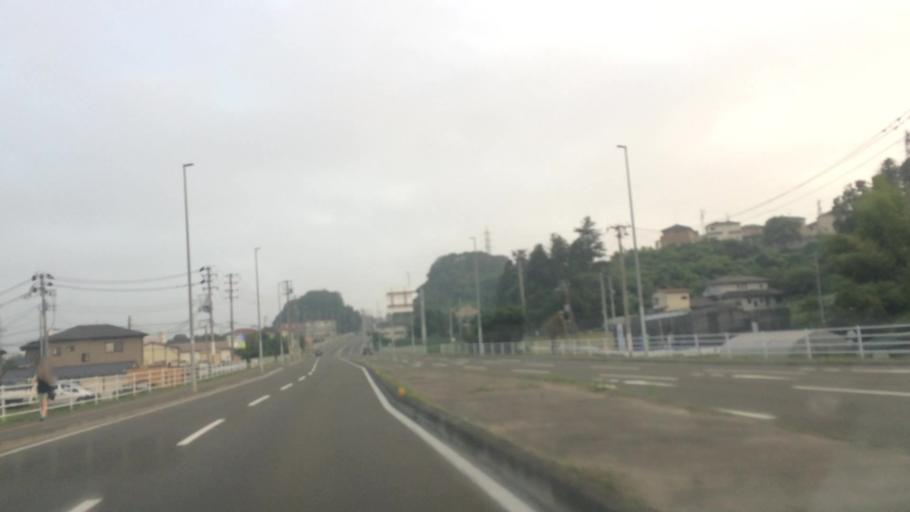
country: JP
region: Miyagi
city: Sendai-shi
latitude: 38.3018
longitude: 140.9202
